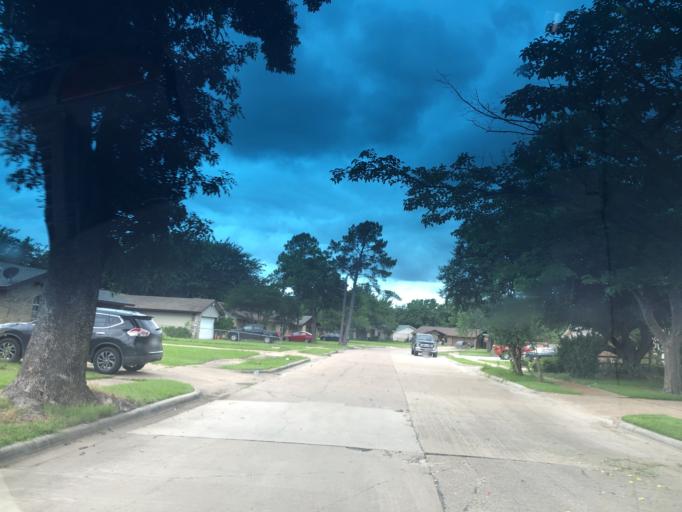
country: US
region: Texas
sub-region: Dallas County
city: Grand Prairie
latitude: 32.7042
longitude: -97.0049
